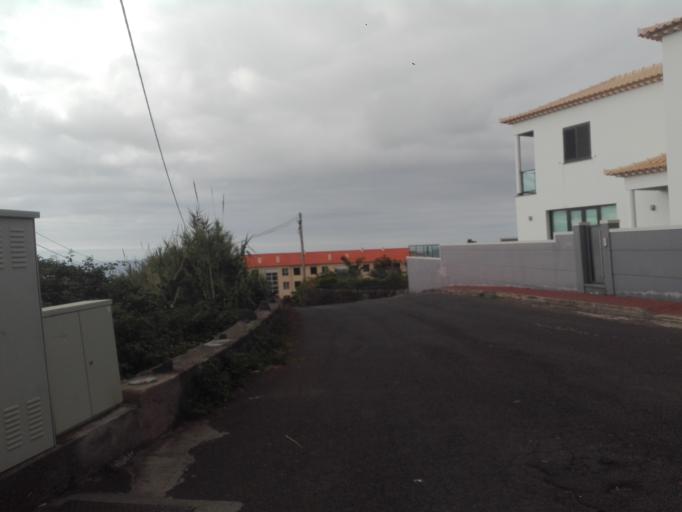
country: PT
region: Madeira
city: Canico
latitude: 32.6538
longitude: -16.8287
